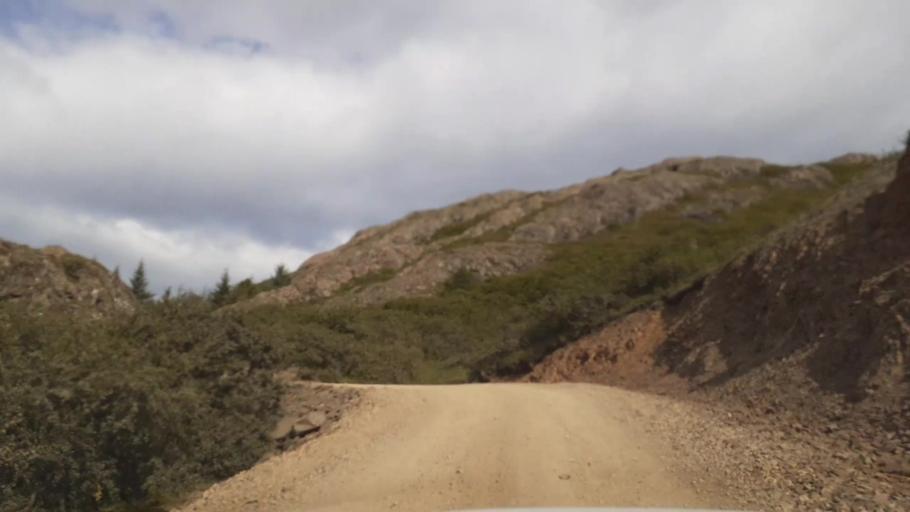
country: IS
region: East
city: Hoefn
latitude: 64.4382
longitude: -14.9124
